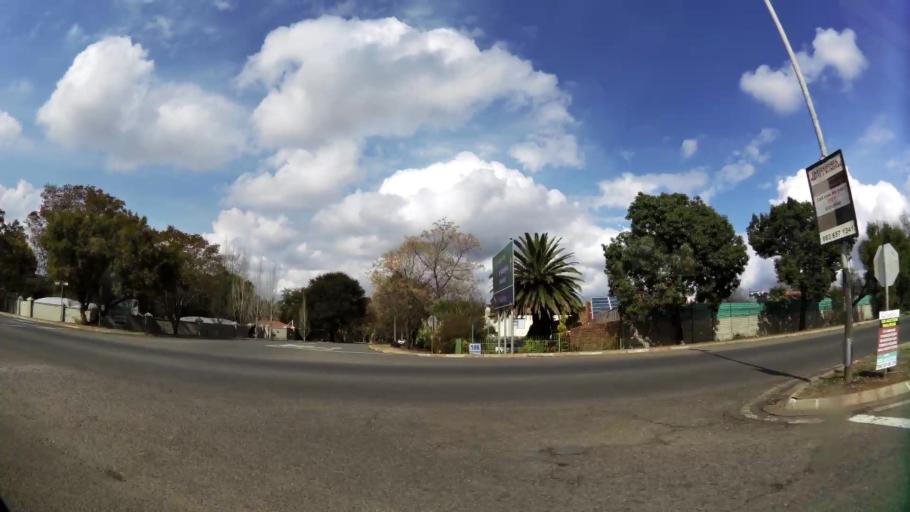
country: ZA
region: Gauteng
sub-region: Sedibeng District Municipality
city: Vanderbijlpark
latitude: -26.7368
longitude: 27.8254
